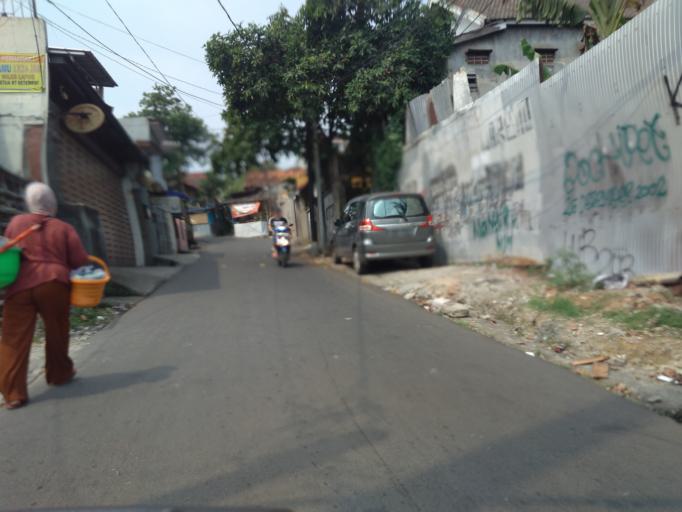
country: ID
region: Jakarta Raya
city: Jakarta
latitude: -6.2565
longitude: 106.7924
